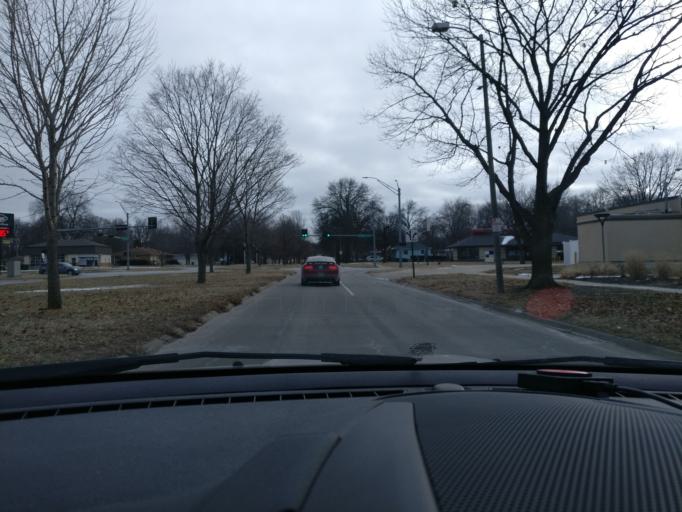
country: US
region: Nebraska
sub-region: Lancaster County
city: Lincoln
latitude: 40.8493
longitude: -96.6402
